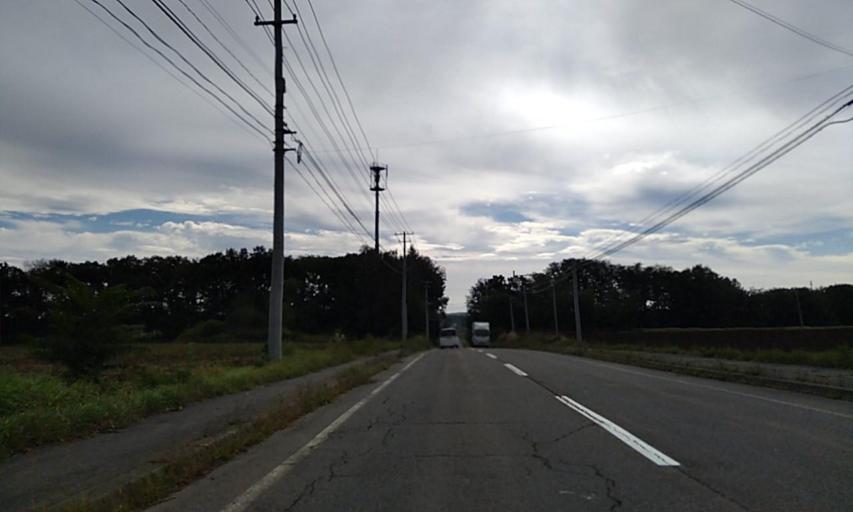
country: JP
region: Hokkaido
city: Obihiro
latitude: 42.8469
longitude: 143.1715
